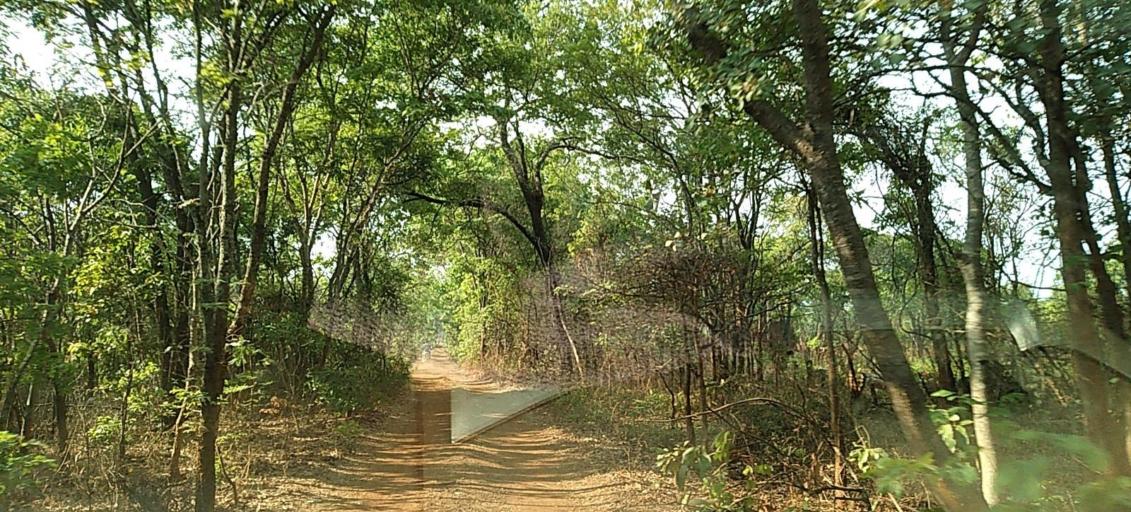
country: ZM
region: Copperbelt
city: Kalulushi
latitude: -12.9718
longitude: 27.7148
